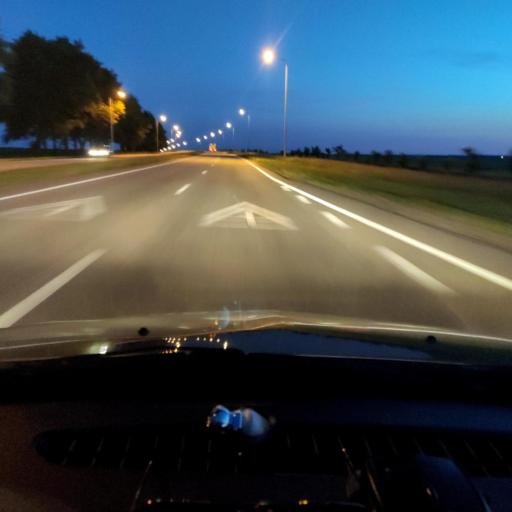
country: RU
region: Belgorod
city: Skorodnoye
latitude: 51.1718
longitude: 37.3216
